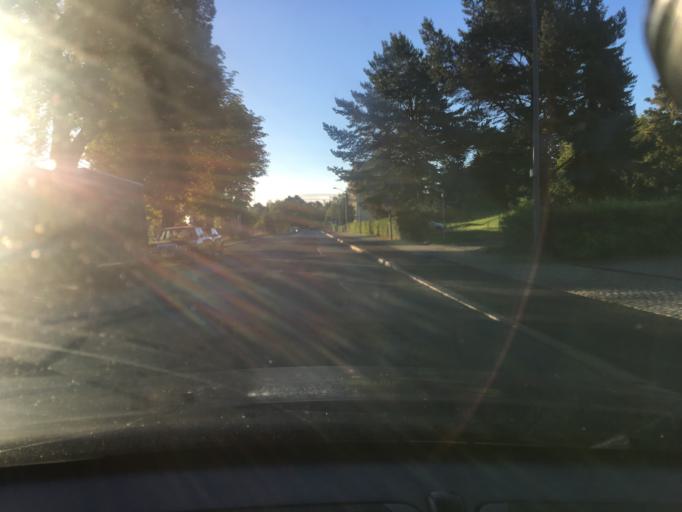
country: DE
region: Saxony
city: Goerlitz
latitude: 51.1443
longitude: 14.9848
